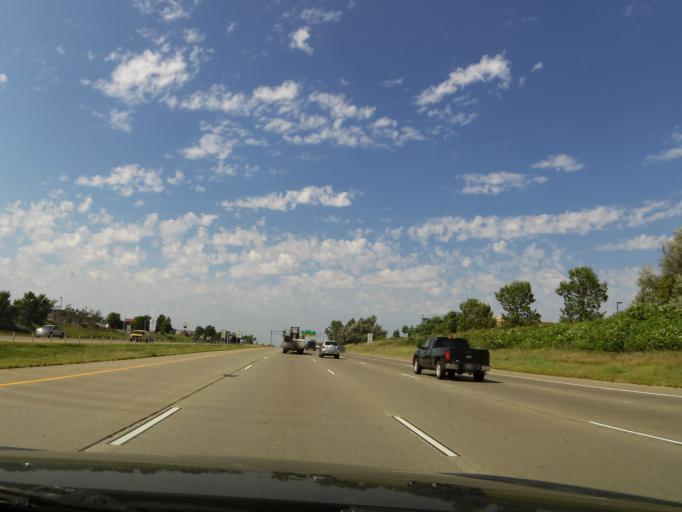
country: US
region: Minnesota
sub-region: Washington County
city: Oakdale
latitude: 44.9488
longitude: -92.9444
